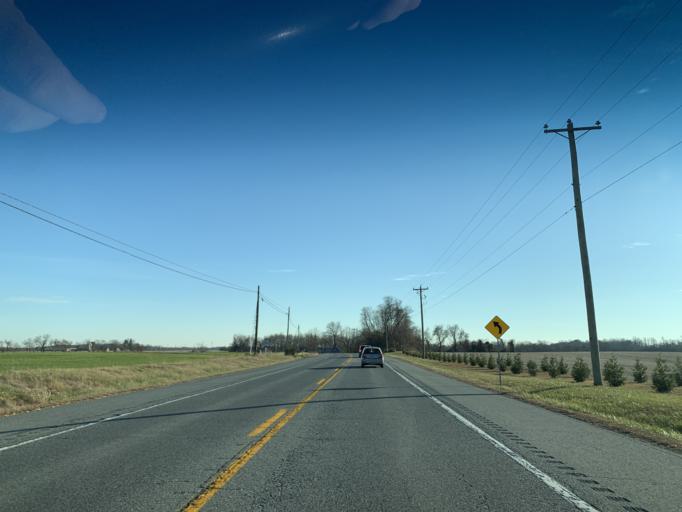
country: US
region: Delaware
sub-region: New Castle County
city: Middletown
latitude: 39.4482
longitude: -75.8693
